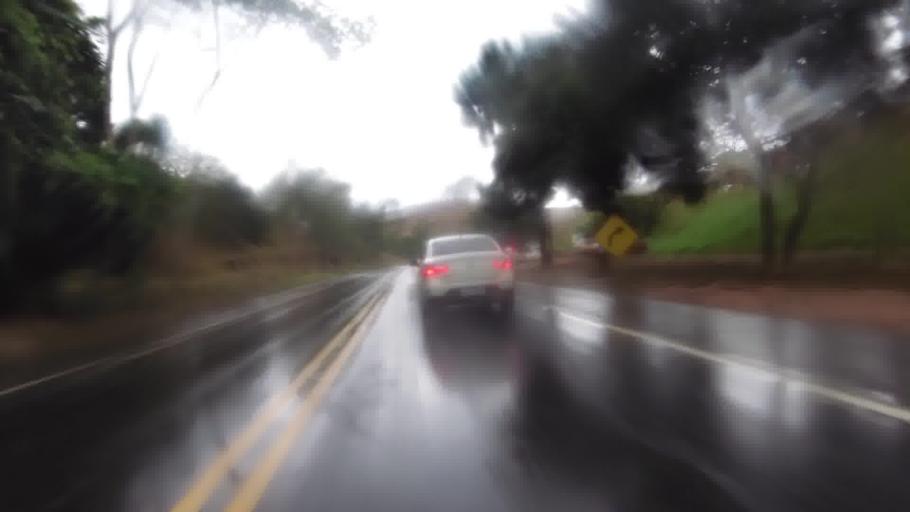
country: BR
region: Espirito Santo
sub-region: Cachoeiro De Itapemirim
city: Cachoeiro de Itapemirim
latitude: -20.9728
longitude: -41.1107
